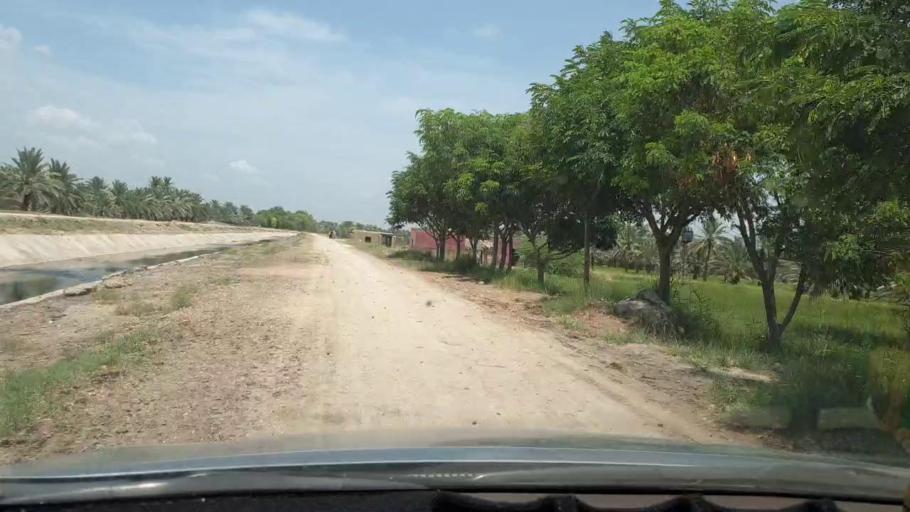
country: PK
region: Sindh
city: Khairpur
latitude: 27.4384
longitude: 68.7820
